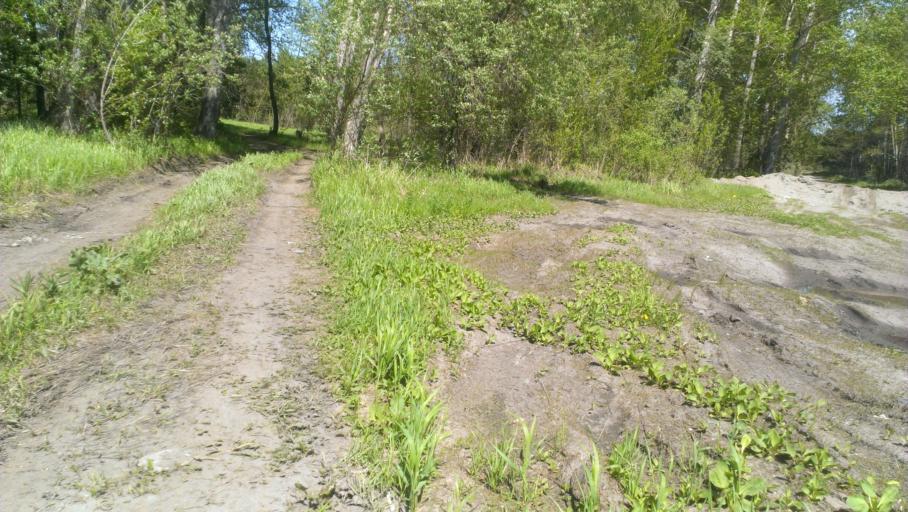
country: RU
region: Altai Krai
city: Zaton
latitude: 53.3134
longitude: 83.8535
